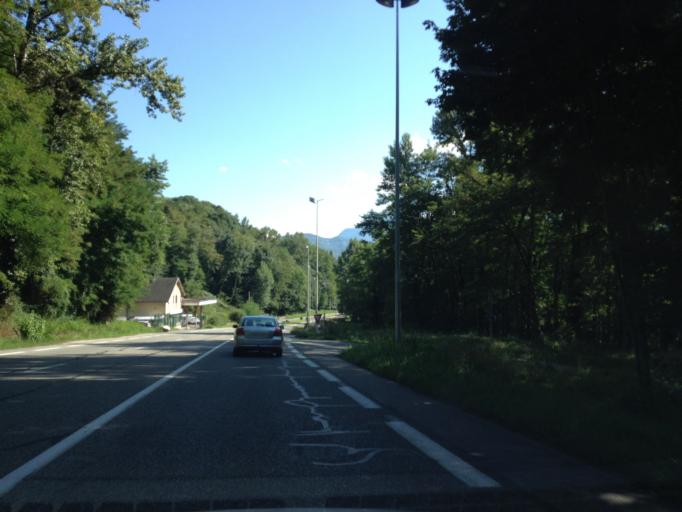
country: FR
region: Rhone-Alpes
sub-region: Departement de la Savoie
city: Cognin
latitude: 45.5900
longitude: 5.9077
